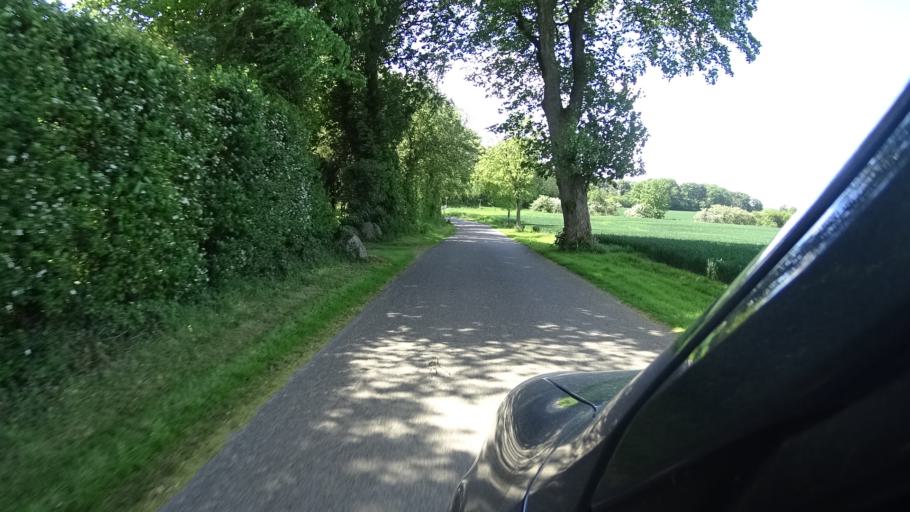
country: DK
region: South Denmark
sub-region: Vejle Kommune
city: Borkop
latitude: 55.6120
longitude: 9.6503
